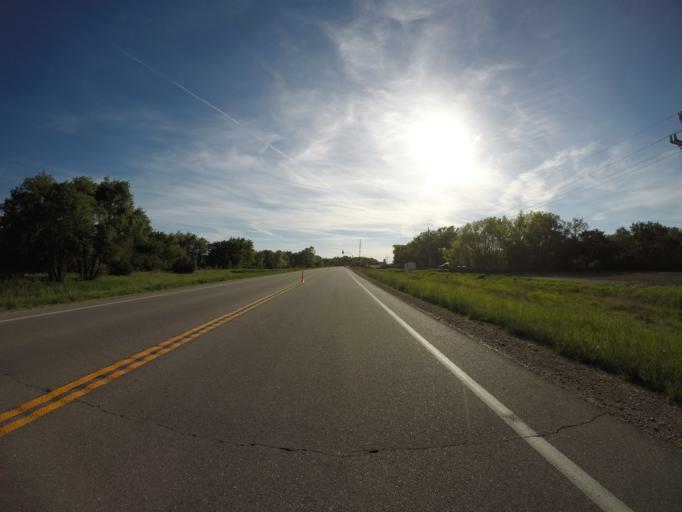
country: US
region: Kansas
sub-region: Cloud County
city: Concordia
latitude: 39.5716
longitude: -97.4337
